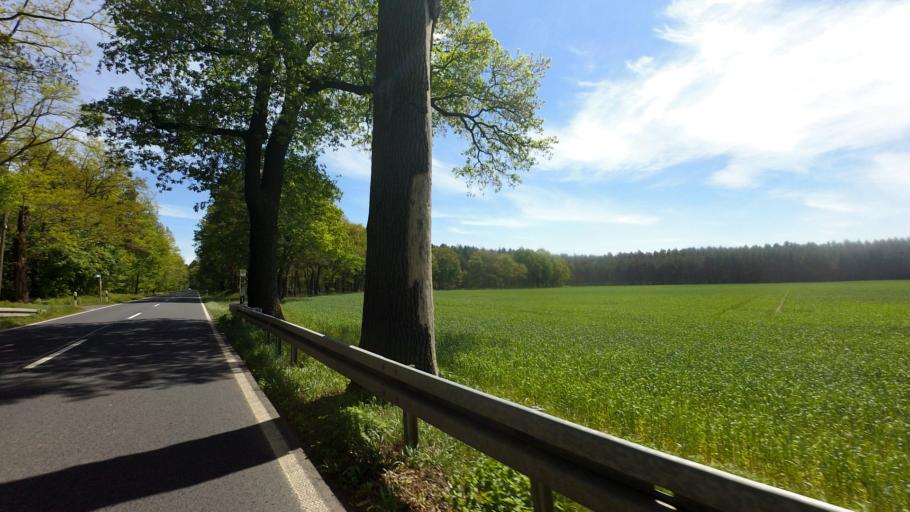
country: DE
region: Brandenburg
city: Luckenwalde
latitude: 52.0512
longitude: 13.2528
